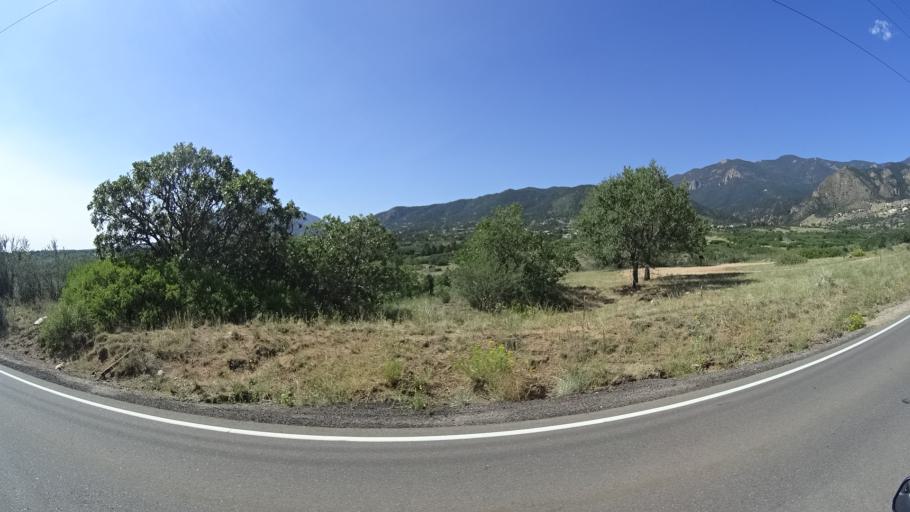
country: US
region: Colorado
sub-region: El Paso County
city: Colorado Springs
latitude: 38.8293
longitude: -104.8658
